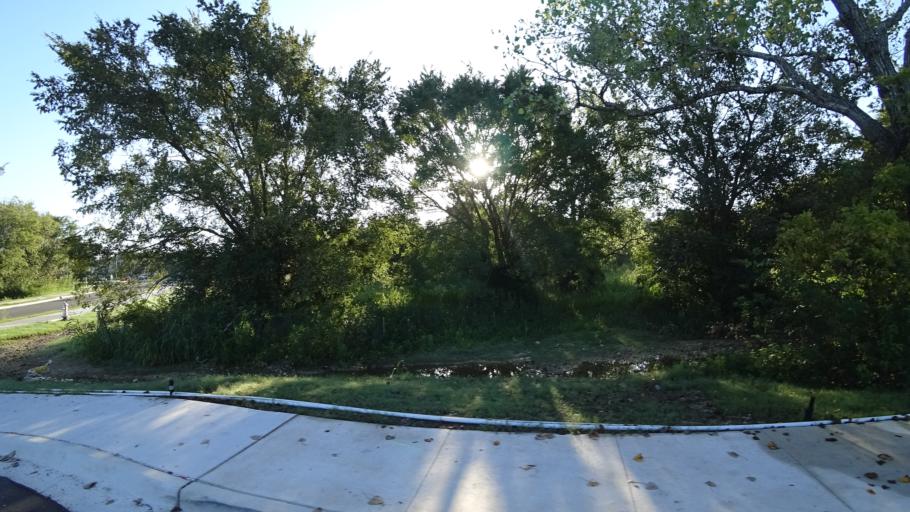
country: US
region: Texas
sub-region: Travis County
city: Wells Branch
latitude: 30.3647
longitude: -97.6870
